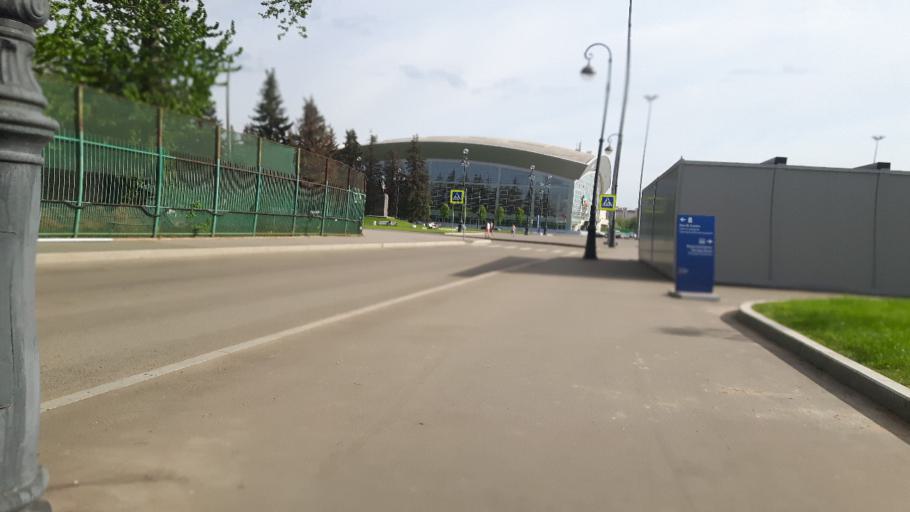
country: RU
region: St.-Petersburg
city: Staraya Derevnya
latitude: 59.9739
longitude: 30.2259
